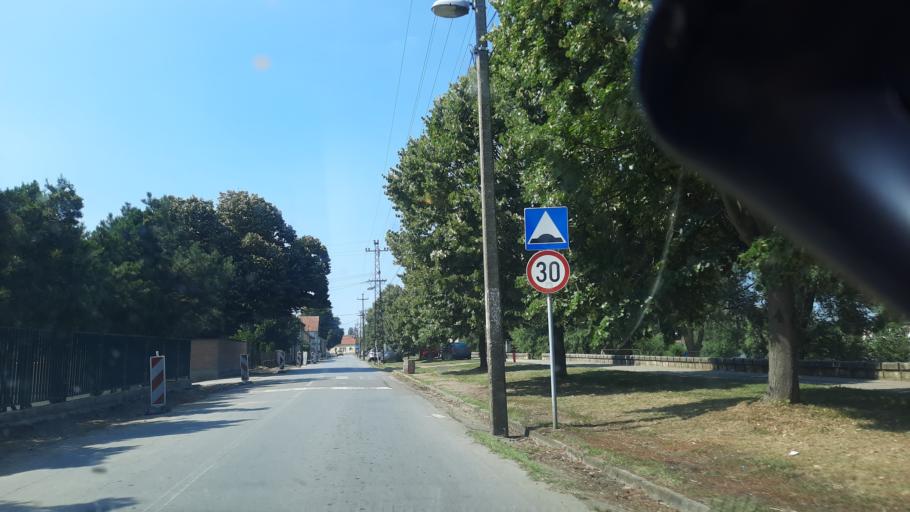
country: RS
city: Macvanska Mitrovica
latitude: 44.9630
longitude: 19.6008
